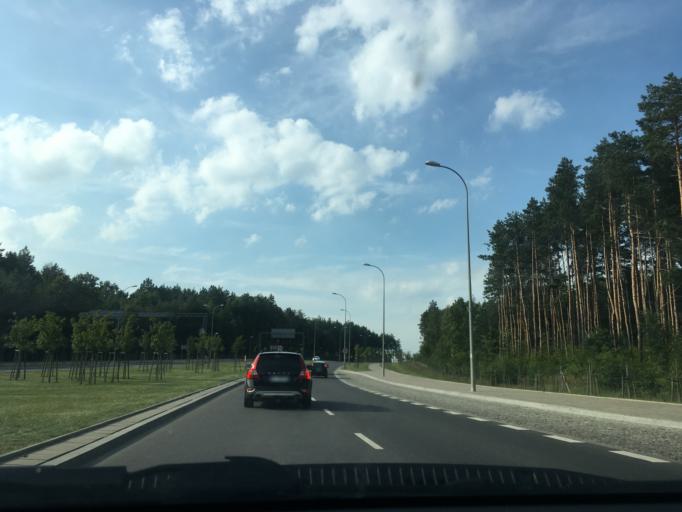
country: PL
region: Podlasie
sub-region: Bialystok
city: Bialystok
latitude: 53.1294
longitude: 23.2233
